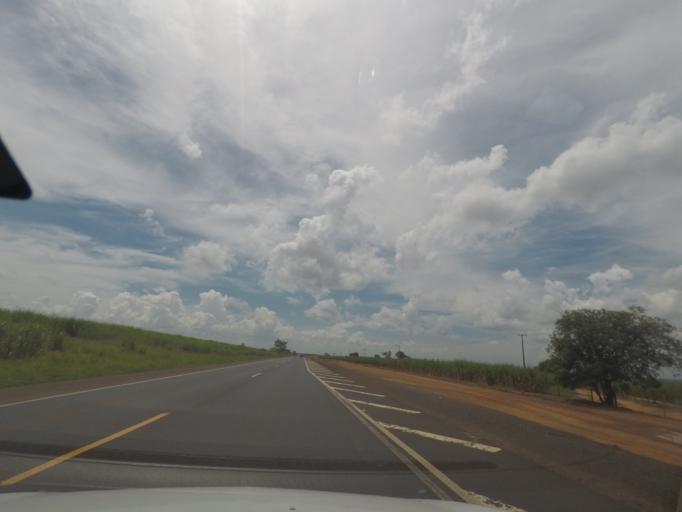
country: BR
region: Sao Paulo
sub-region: Barretos
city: Barretos
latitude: -20.3905
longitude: -48.6397
